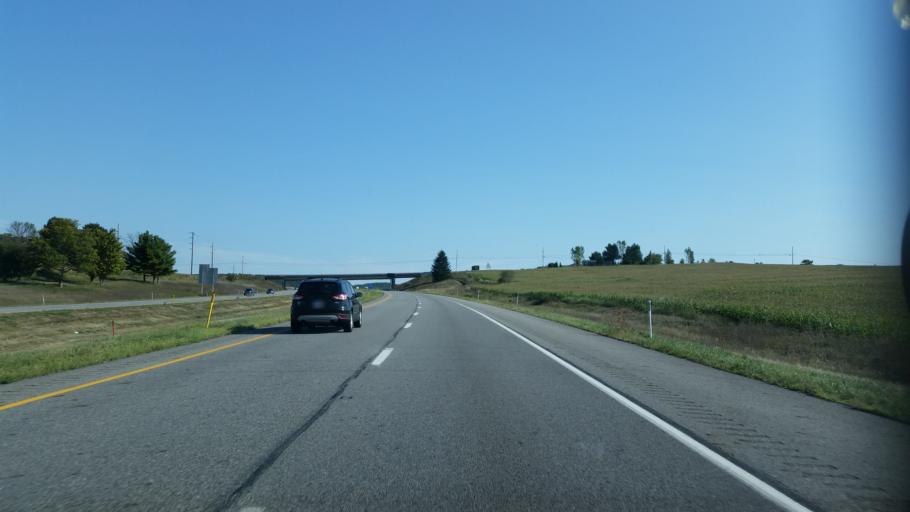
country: US
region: Pennsylvania
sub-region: Bedford County
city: Bedford
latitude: 40.0788
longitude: -78.5267
